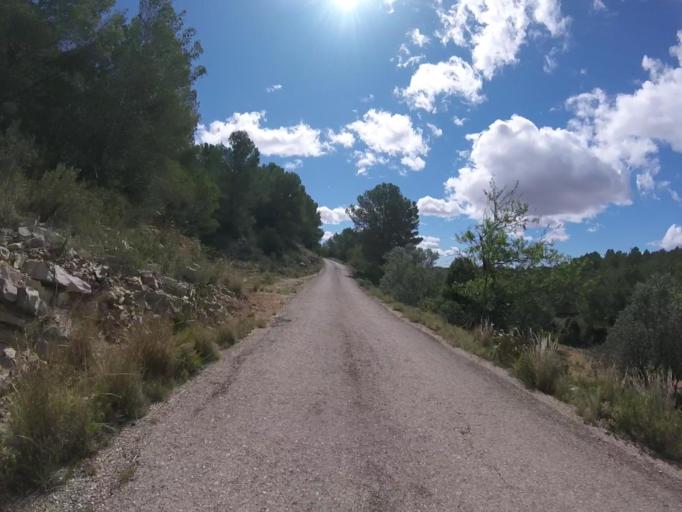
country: ES
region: Valencia
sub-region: Provincia de Castello
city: Adzaneta
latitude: 40.2699
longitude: -0.1061
